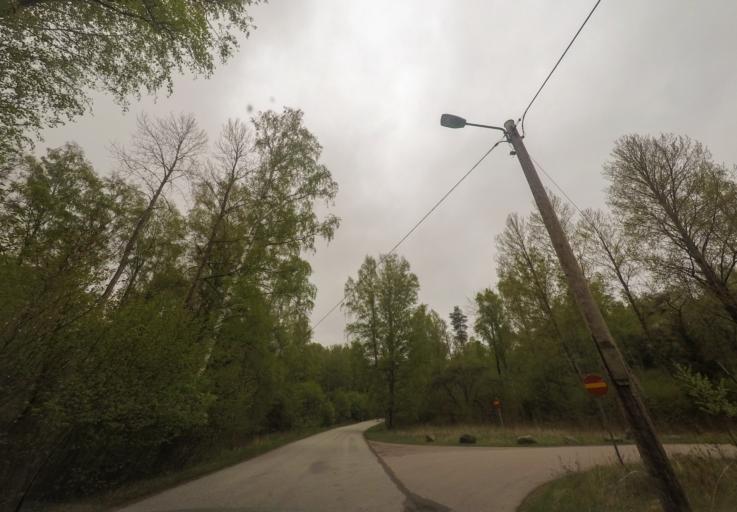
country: SE
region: Vaestmanland
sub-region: Vasteras
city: Vasteras
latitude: 59.5754
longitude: 16.6121
